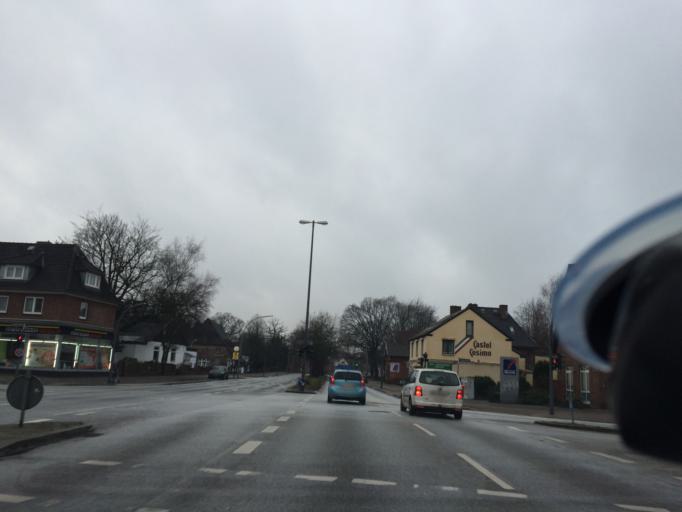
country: DE
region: Schleswig-Holstein
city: Halstenbek
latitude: 53.5729
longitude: 9.8470
